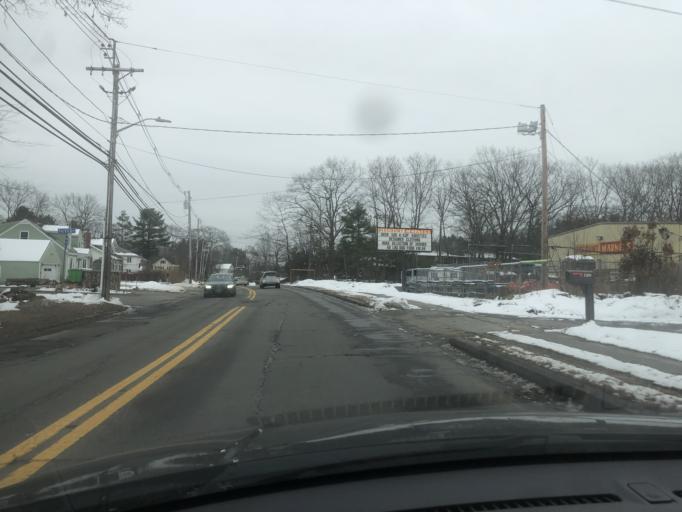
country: US
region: Massachusetts
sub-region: Middlesex County
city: Tewksbury
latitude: 42.6043
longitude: -71.2245
